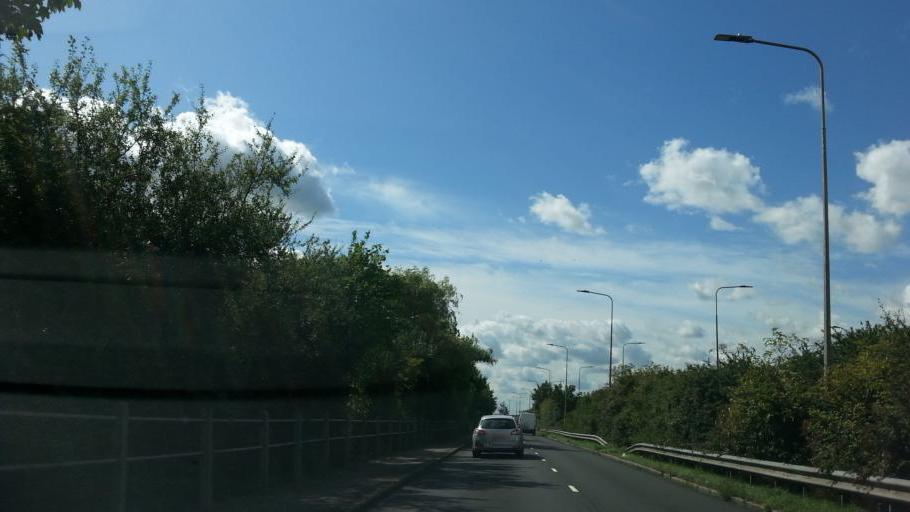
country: GB
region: England
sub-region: Essex
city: Canvey Island
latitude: 51.5274
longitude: 0.5590
